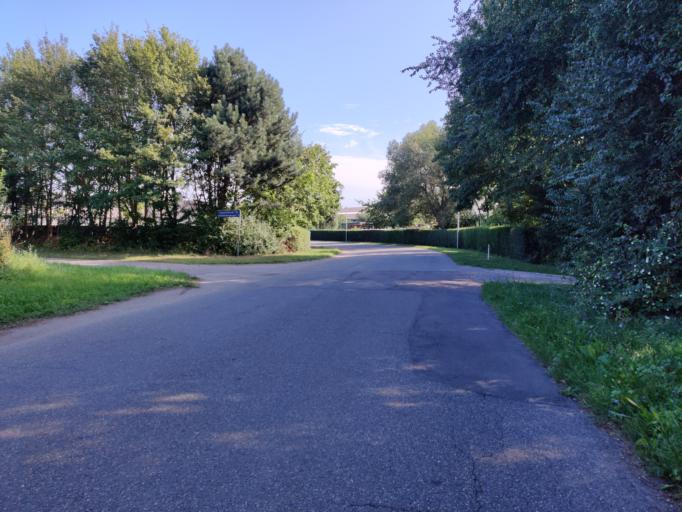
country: DK
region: Zealand
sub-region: Guldborgsund Kommune
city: Nykobing Falster
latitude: 54.7206
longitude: 11.9270
